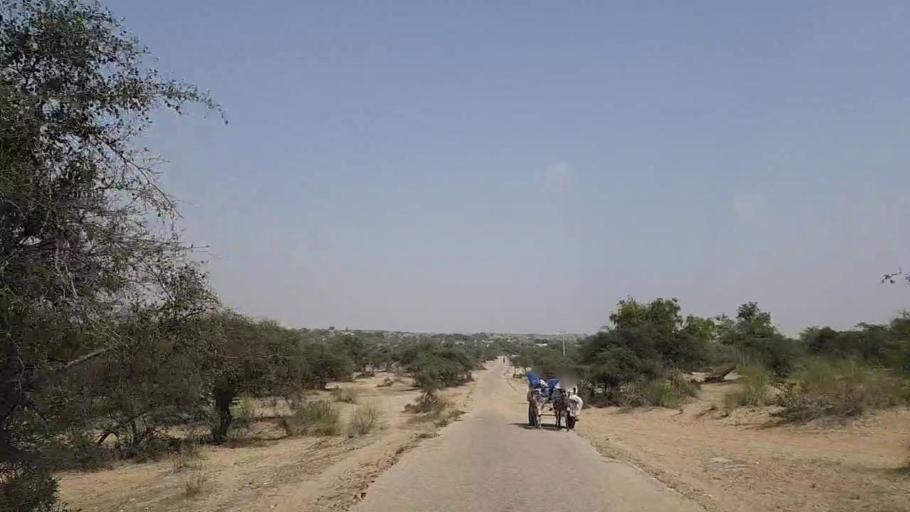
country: PK
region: Sindh
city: Mithi
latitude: 24.7571
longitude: 69.9262
